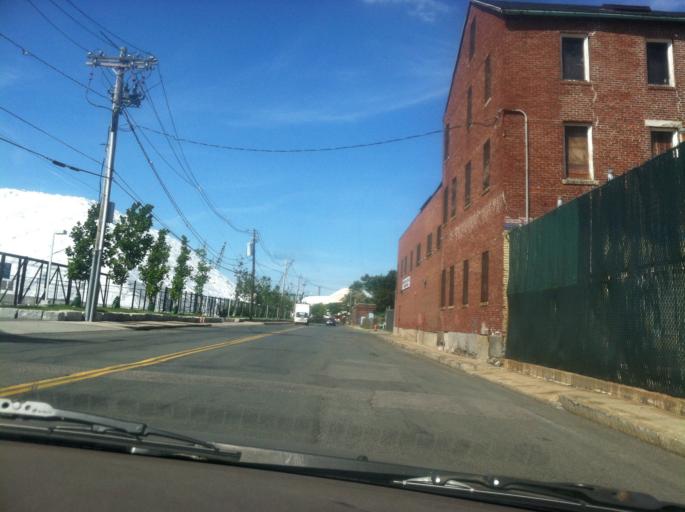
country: US
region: Massachusetts
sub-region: Suffolk County
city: Chelsea
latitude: 42.3848
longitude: -71.0205
